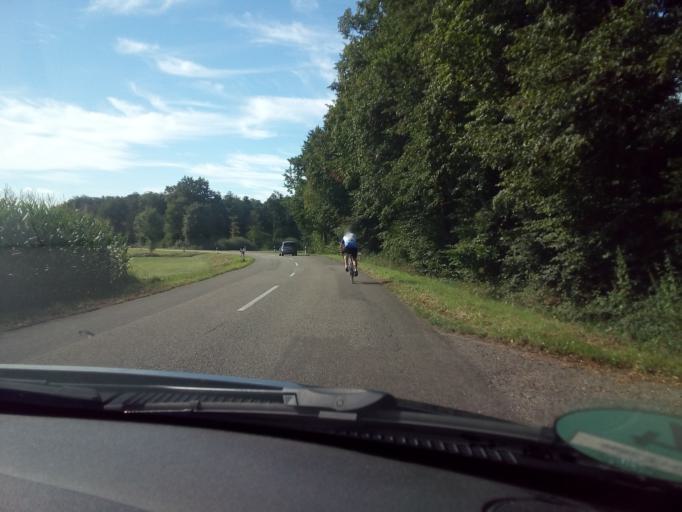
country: DE
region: Baden-Wuerttemberg
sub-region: Karlsruhe Region
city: Lichtenau
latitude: 48.6718
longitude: 8.0051
